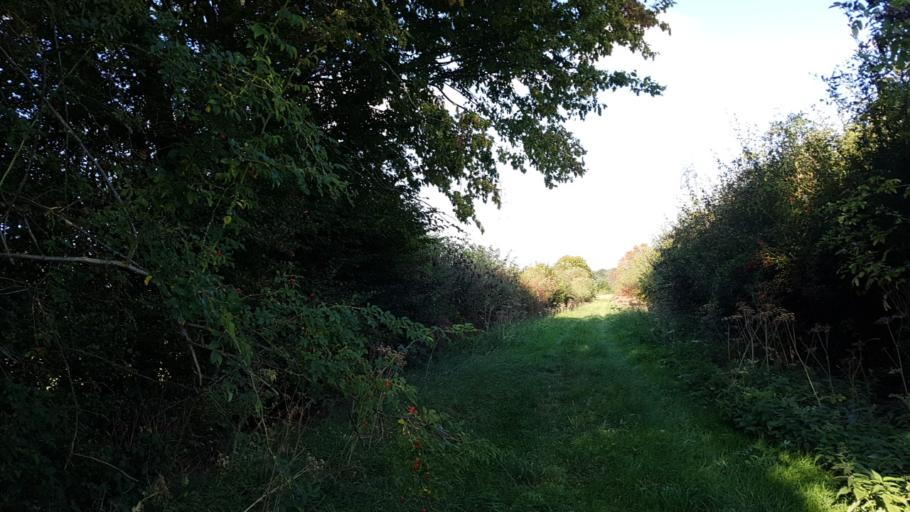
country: FR
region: Picardie
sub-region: Departement de l'Aisne
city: La Capelle
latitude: 49.9805
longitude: 3.9273
